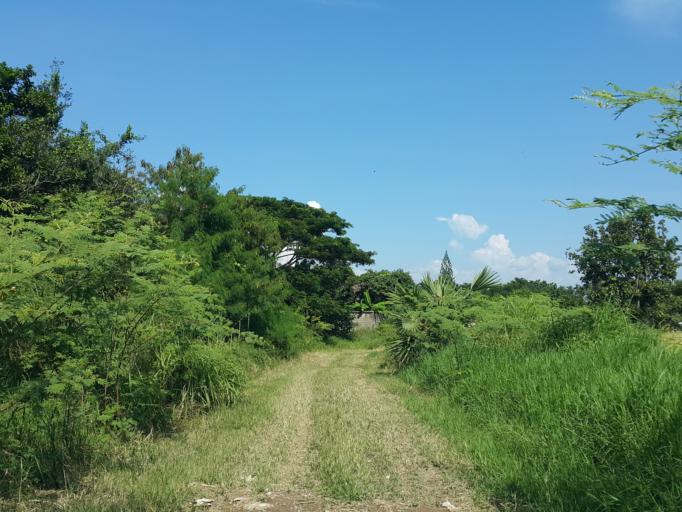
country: TH
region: Chiang Mai
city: Saraphi
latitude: 18.7697
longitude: 99.0587
